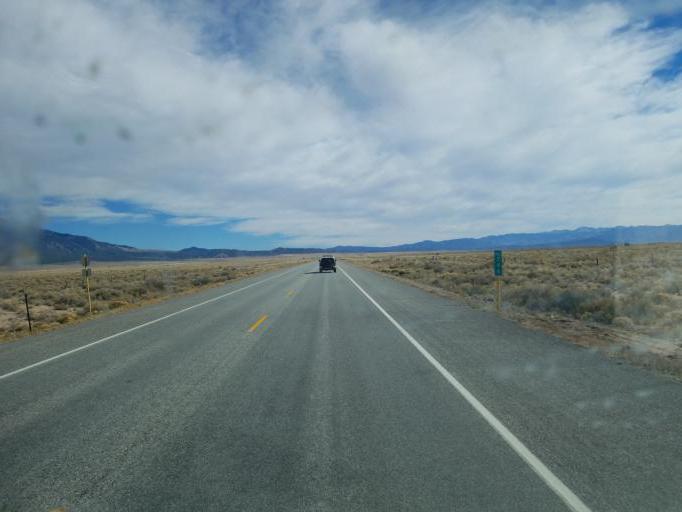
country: US
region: Colorado
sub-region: Alamosa County
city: Alamosa East
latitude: 37.4750
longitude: -105.6372
